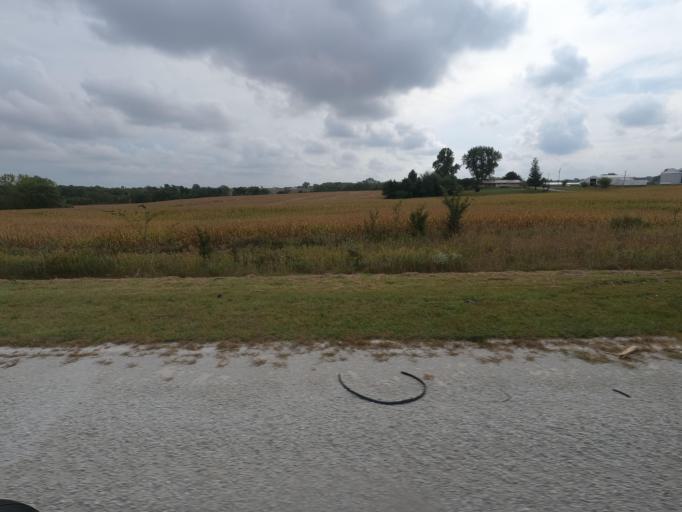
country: US
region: Iowa
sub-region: Wapello County
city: Ottumwa
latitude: 41.0038
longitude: -92.2896
